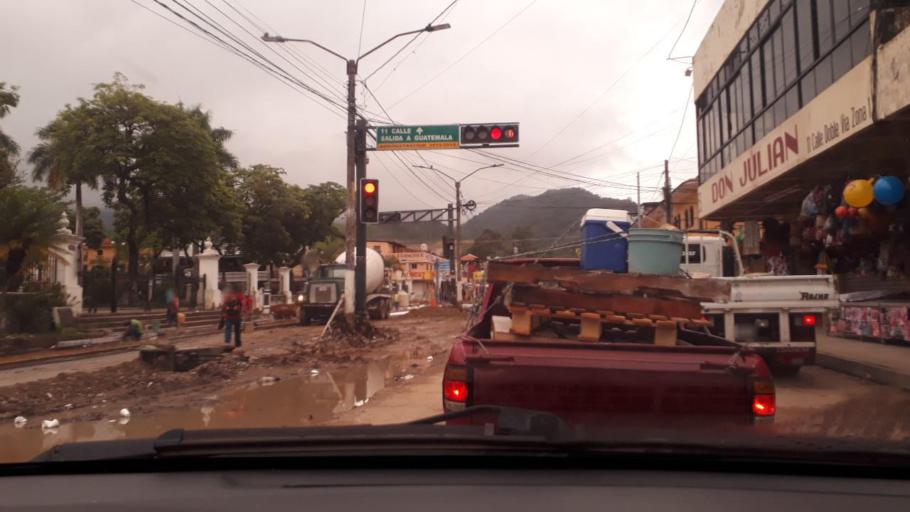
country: GT
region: Chiquimula
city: Esquipulas
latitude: 14.5634
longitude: -89.3515
